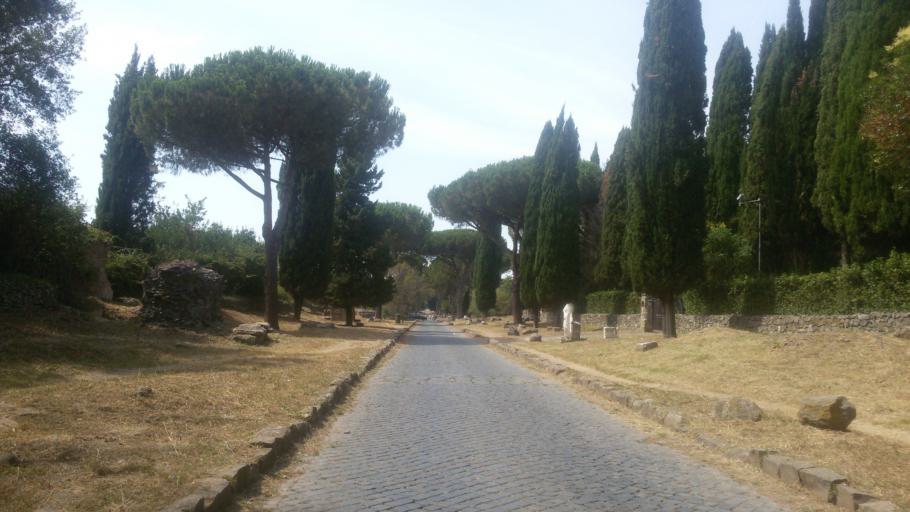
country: IT
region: Latium
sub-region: Citta metropolitana di Roma Capitale
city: Rome
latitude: 41.8332
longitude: 12.5418
